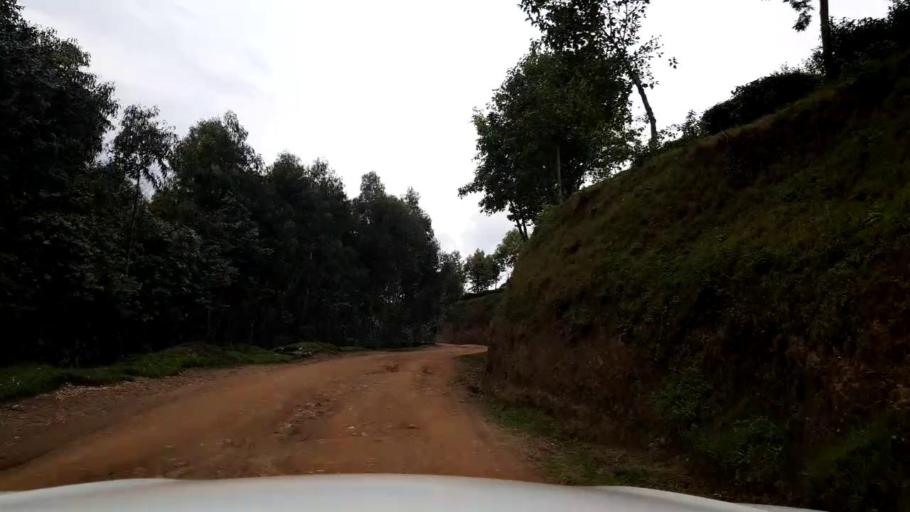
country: RW
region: Western Province
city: Kibuye
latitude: -1.9566
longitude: 29.4029
